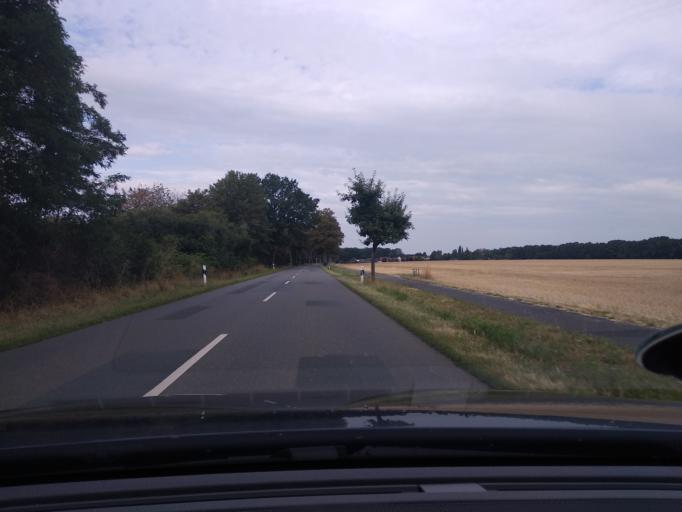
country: DE
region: Lower Saxony
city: Wagenhoff
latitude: 52.5094
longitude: 10.4980
